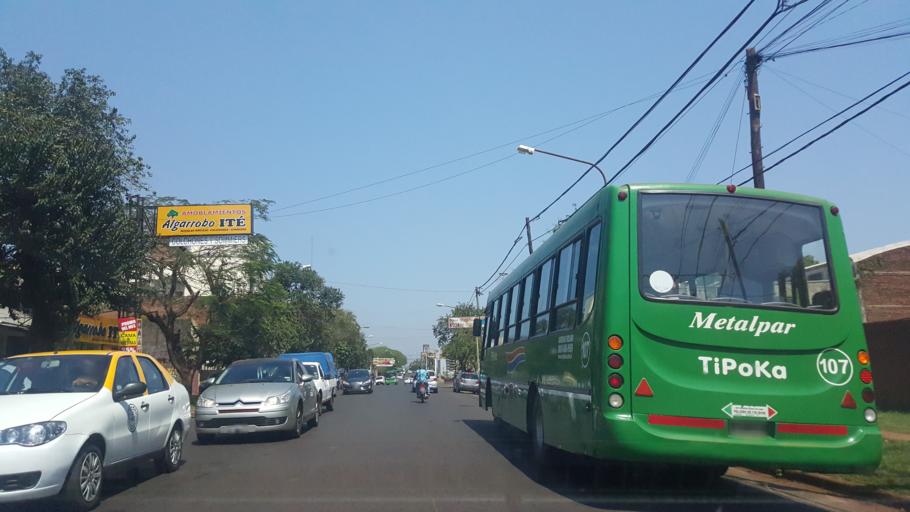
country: AR
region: Misiones
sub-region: Departamento de Capital
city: Posadas
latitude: -27.3902
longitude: -55.9083
